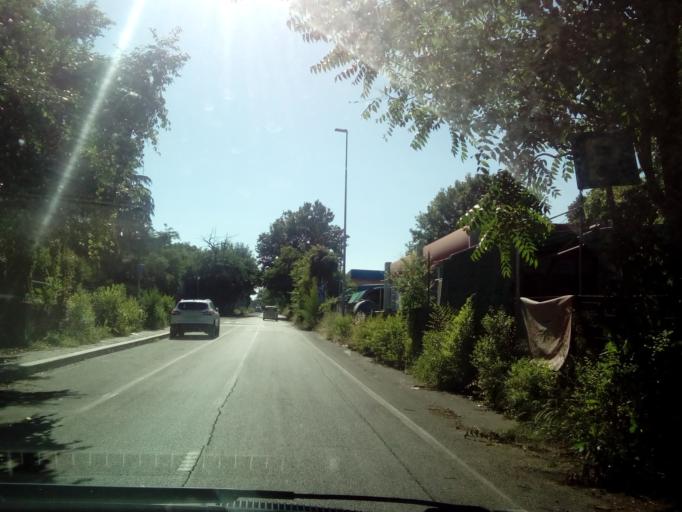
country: IT
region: Latium
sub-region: Citta metropolitana di Roma Capitale
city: Rome
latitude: 41.8948
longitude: 12.5725
